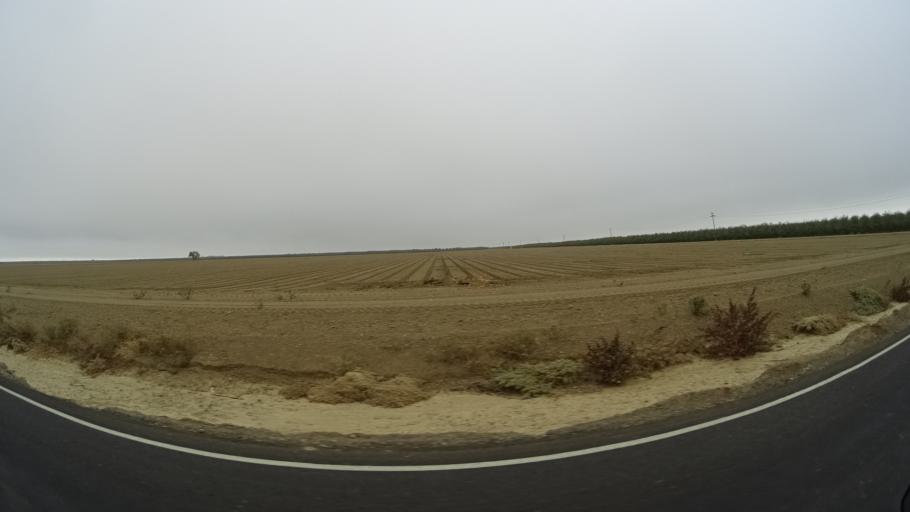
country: US
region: California
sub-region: Yolo County
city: Dunnigan
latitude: 38.9260
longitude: -122.0252
